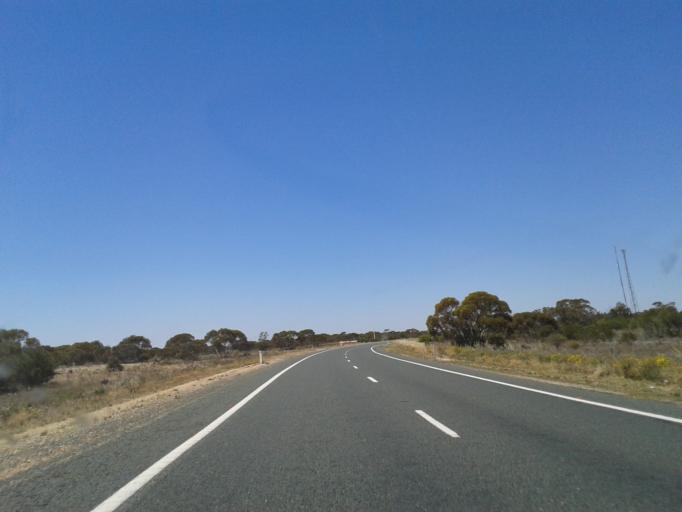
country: AU
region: New South Wales
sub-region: Wentworth
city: Gol Gol
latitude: -34.3186
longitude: 142.3868
